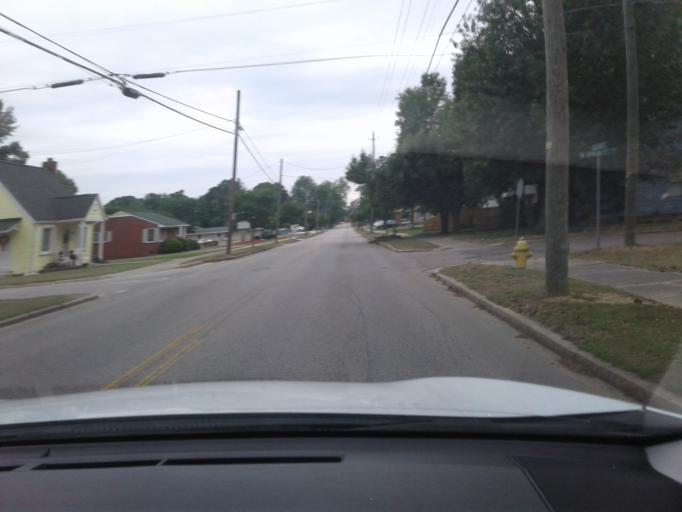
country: US
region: North Carolina
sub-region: Harnett County
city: Dunn
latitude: 35.3163
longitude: -78.6112
